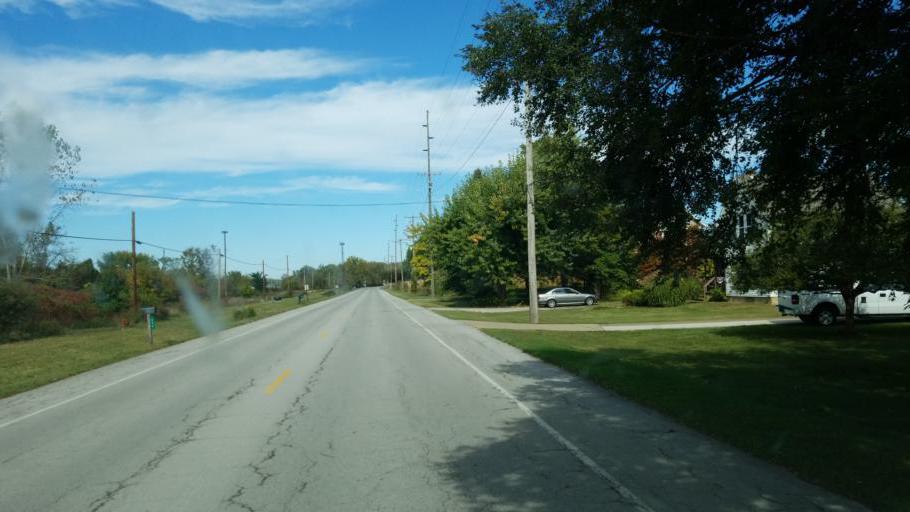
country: US
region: Ohio
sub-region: Erie County
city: Huron
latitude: 41.3808
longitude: -82.5481
